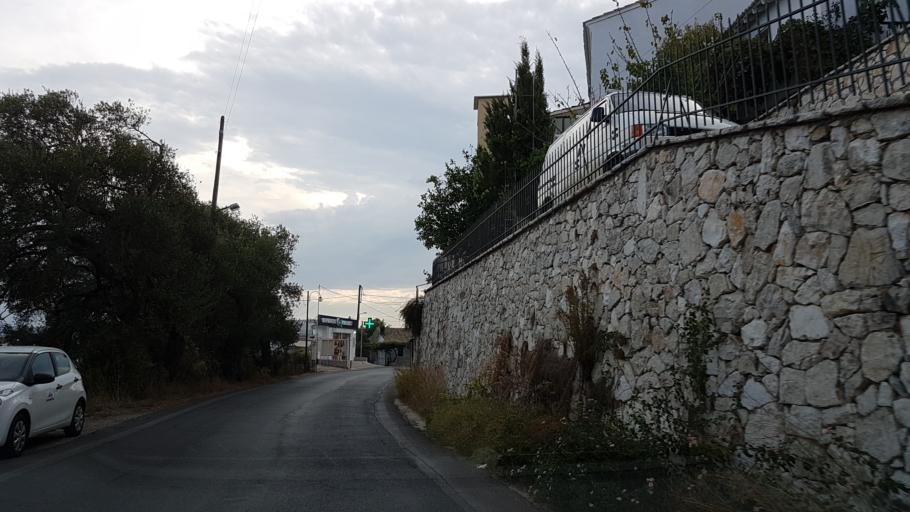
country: GR
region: Ionian Islands
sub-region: Nomos Kerkyras
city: Kontokali
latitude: 39.7271
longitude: 19.9058
